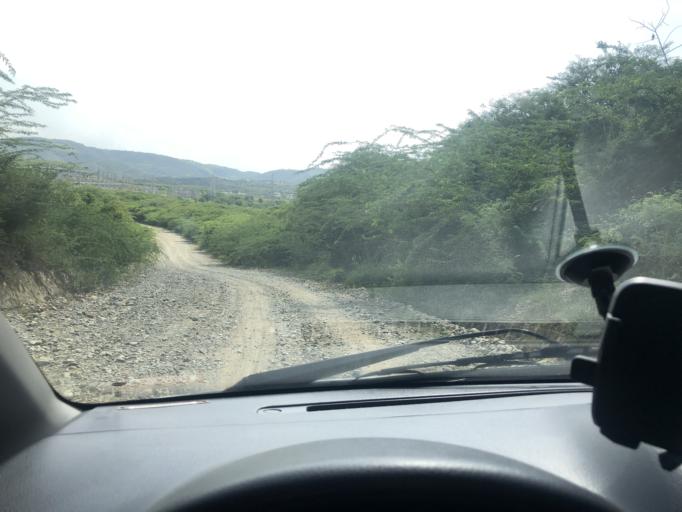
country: DO
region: Santiago
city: Santiago de los Caballeros
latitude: 19.4111
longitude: -70.7533
